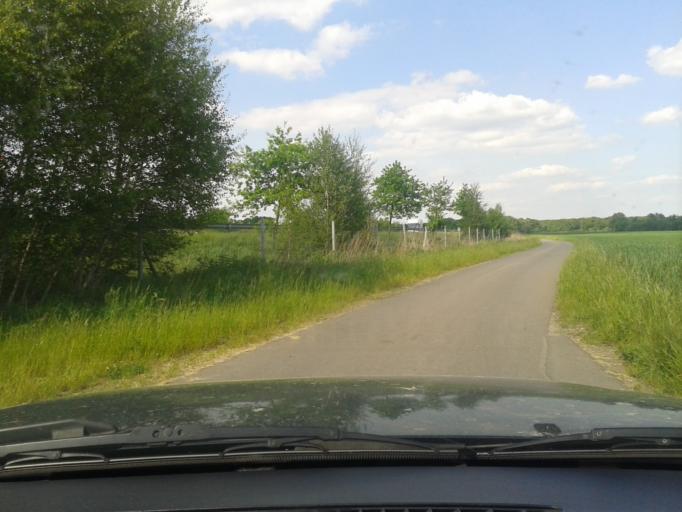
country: DE
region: Lower Saxony
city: Adelheidsdorf
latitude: 52.5384
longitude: 10.0694
